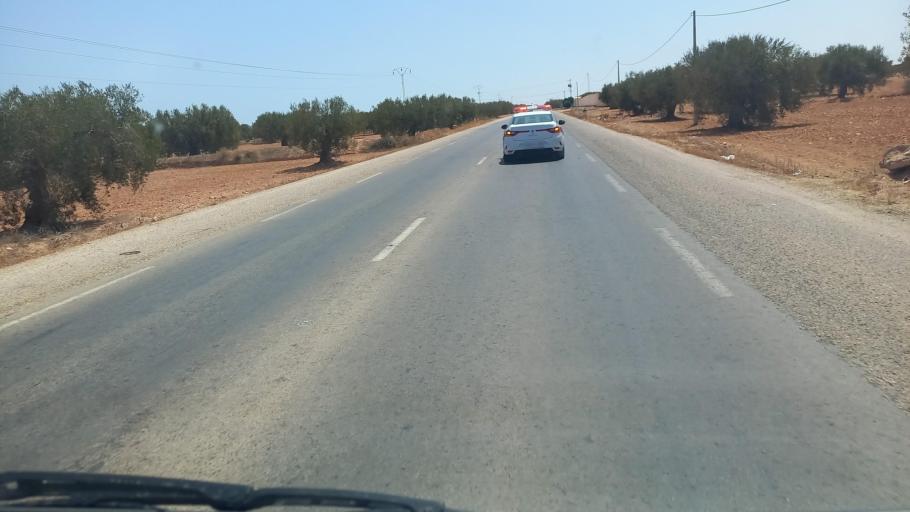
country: TN
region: Madanin
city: Zarzis
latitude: 33.5642
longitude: 11.0506
